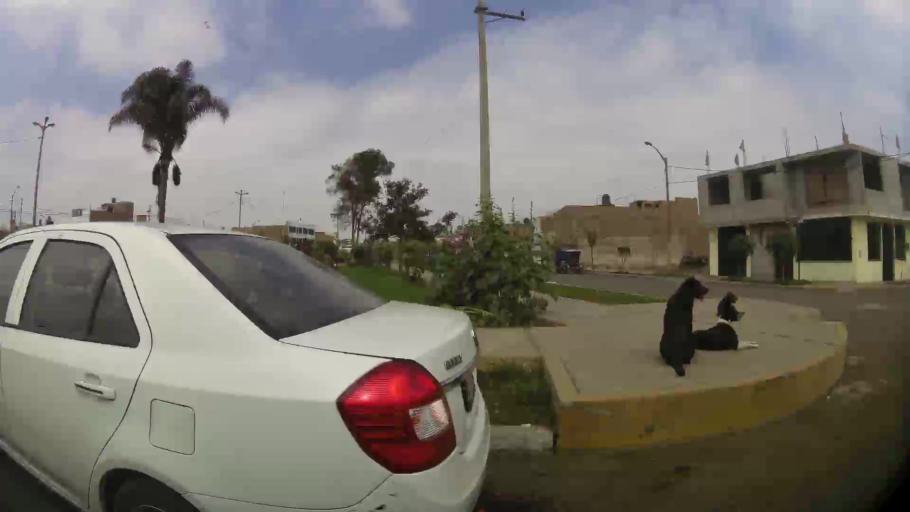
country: PE
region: Lima
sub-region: Provincia de Huaral
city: Huaral
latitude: -11.4943
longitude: -77.2163
